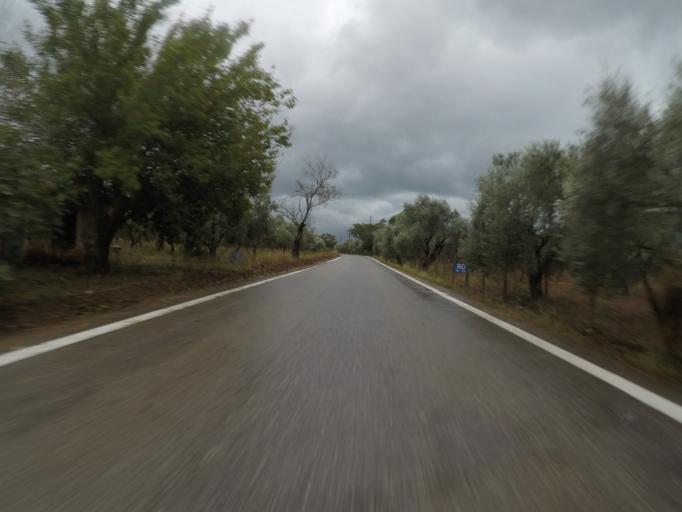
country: GR
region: Peloponnese
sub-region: Nomos Messinias
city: Pylos
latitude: 36.9822
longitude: 21.6847
